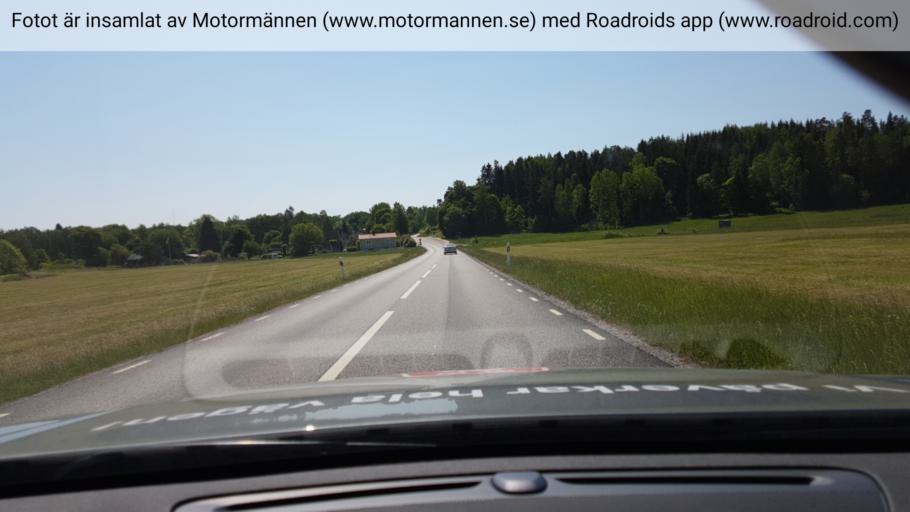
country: SE
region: Stockholm
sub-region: Norrtalje Kommun
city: Rimbo
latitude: 59.7029
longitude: 18.3730
